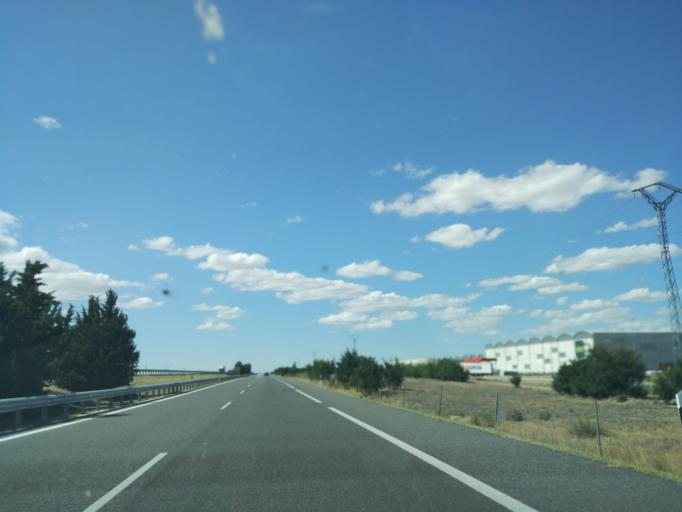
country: ES
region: Castille and Leon
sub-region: Provincia de Valladolid
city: San Vicente del Palacio
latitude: 41.2544
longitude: -4.8732
